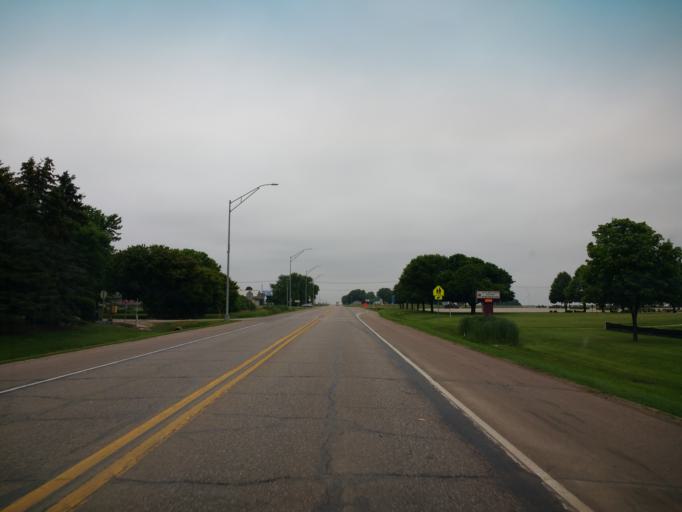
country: US
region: Iowa
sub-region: O'Brien County
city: Hartley
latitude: 43.1849
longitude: -95.4840
